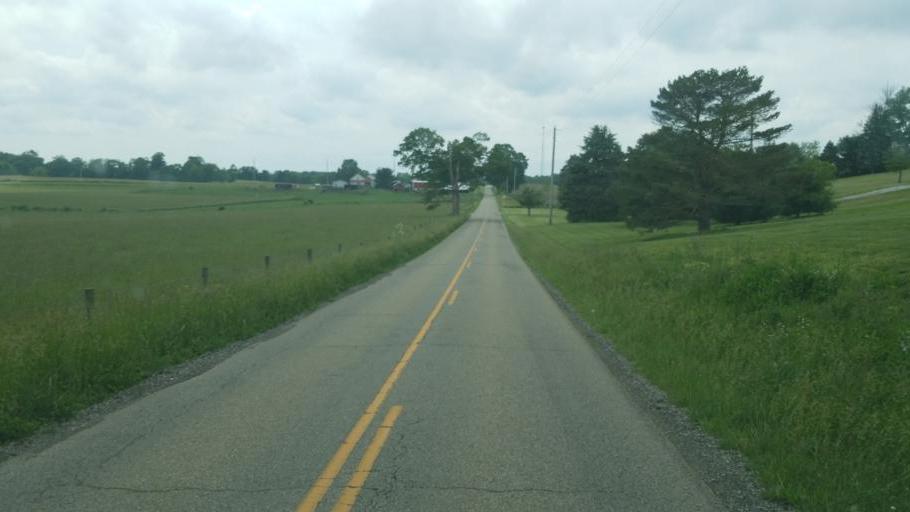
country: US
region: Ohio
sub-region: Perry County
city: Thornport
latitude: 39.9211
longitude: -82.3947
